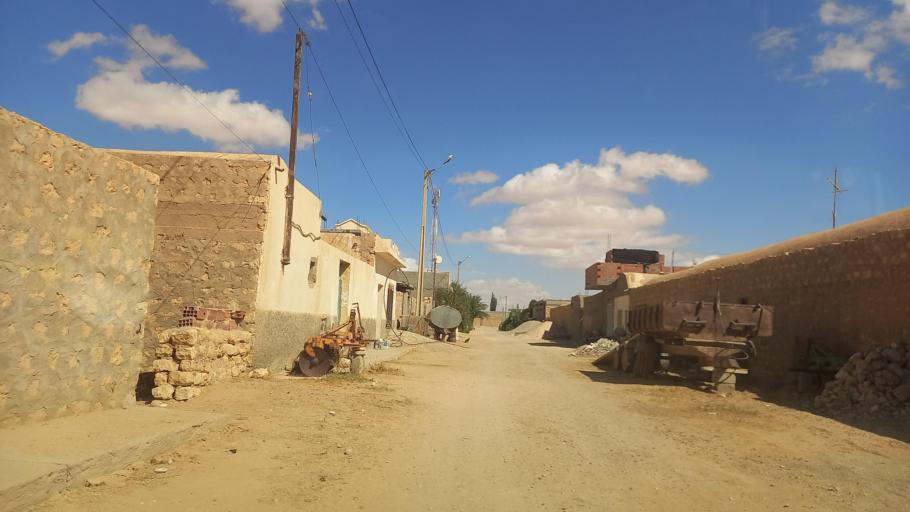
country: TN
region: Tataouine
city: Tataouine
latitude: 32.6952
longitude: 10.3285
